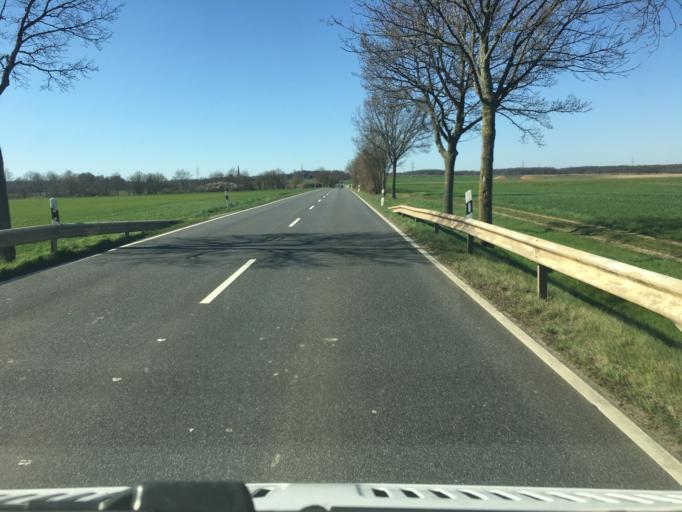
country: DE
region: North Rhine-Westphalia
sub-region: Regierungsbezirk Koln
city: Vettweiss
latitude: 50.7412
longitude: 6.5705
